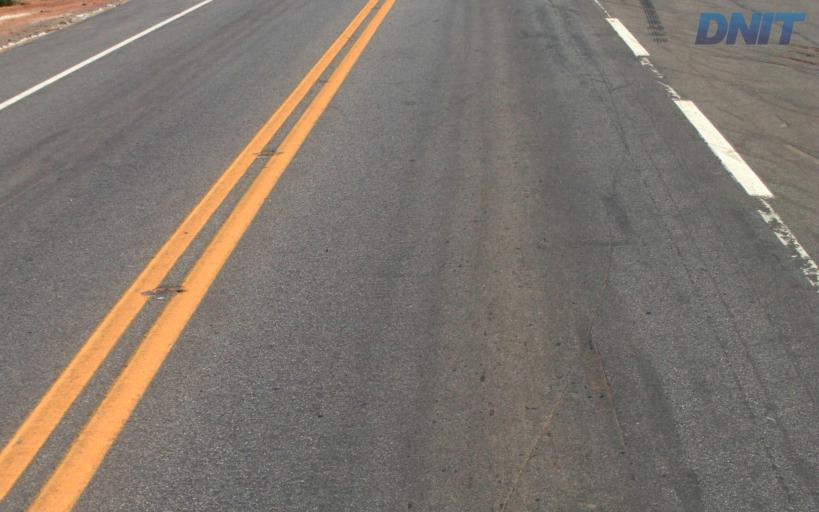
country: BR
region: Minas Gerais
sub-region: Governador Valadares
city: Governador Valadares
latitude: -18.8952
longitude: -42.0046
